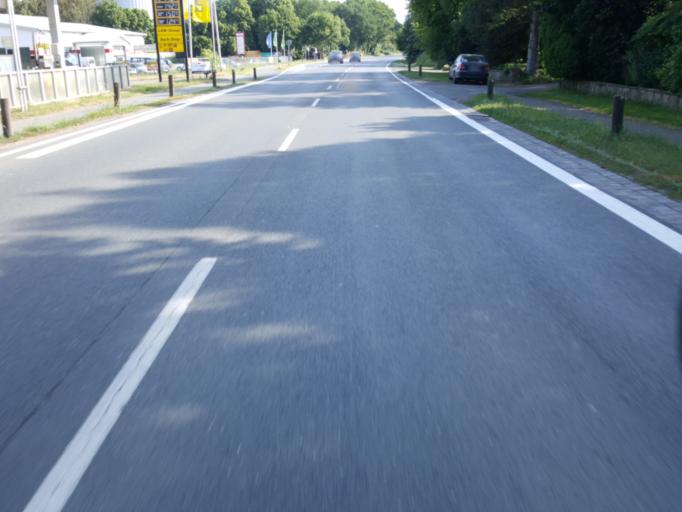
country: DE
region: Lower Saxony
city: Estorf
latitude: 52.5989
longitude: 9.1556
